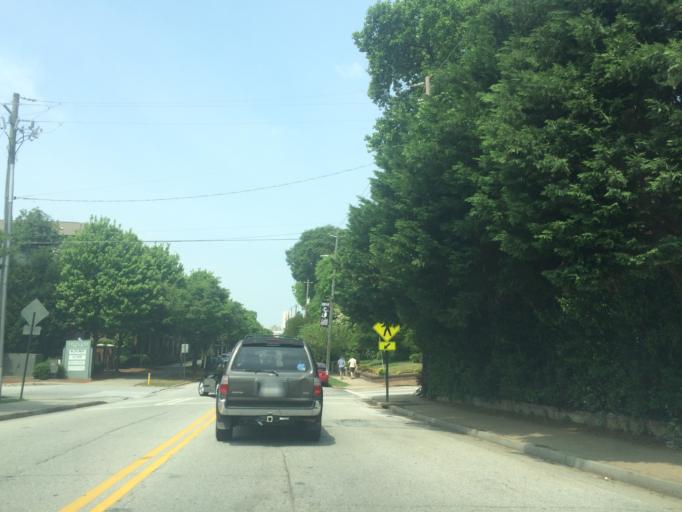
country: US
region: Georgia
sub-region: Fulton County
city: Atlanta
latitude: 33.7613
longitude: -84.3623
